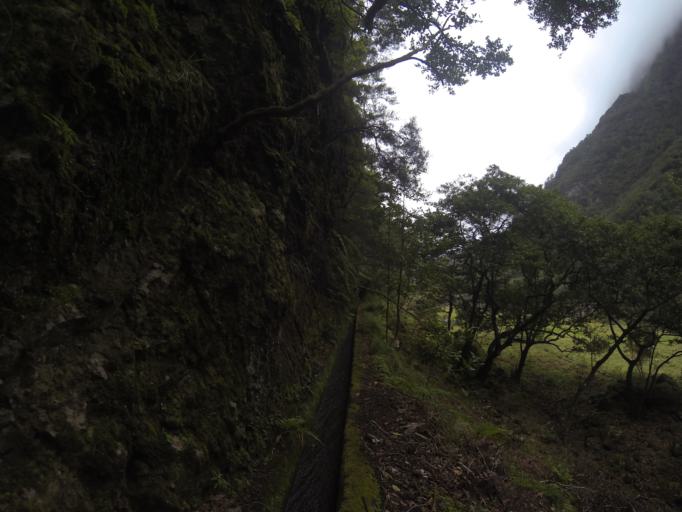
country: PT
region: Madeira
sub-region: Sao Vicente
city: Sao Vicente
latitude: 32.7934
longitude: -17.1133
